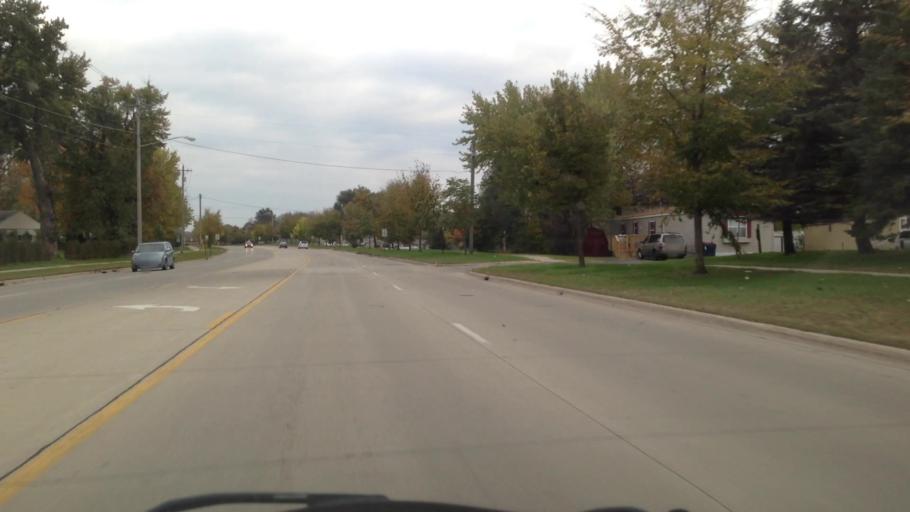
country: US
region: Minnesota
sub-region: Olmsted County
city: Rochester
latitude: 44.0044
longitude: -92.4389
